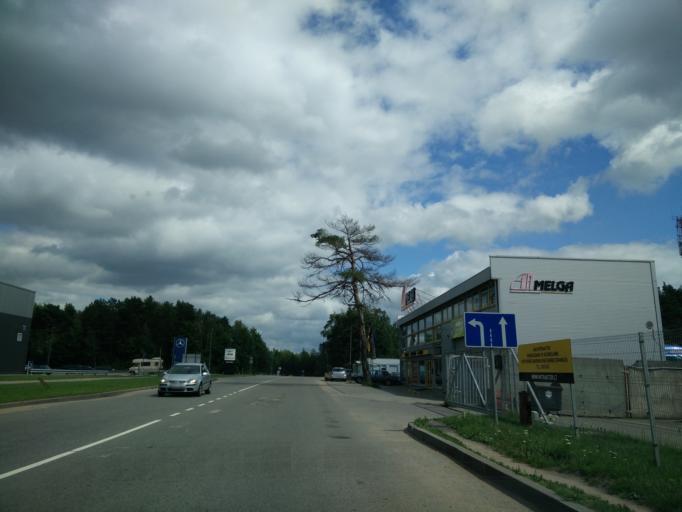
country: LT
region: Vilnius County
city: Pilaite
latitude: 54.6542
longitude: 25.1466
